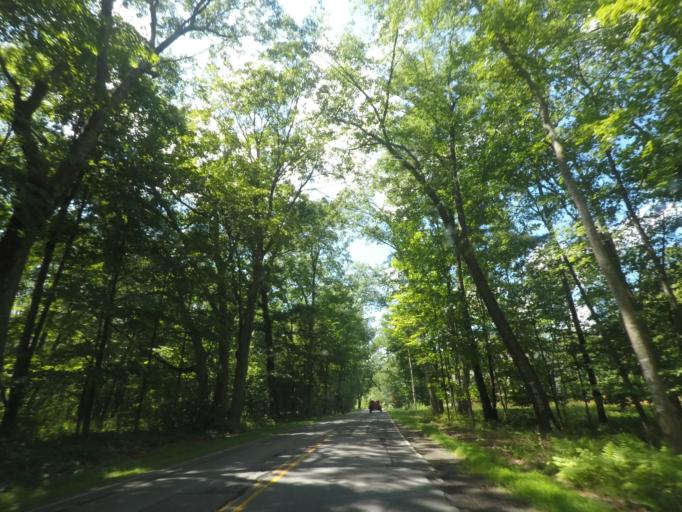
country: US
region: New York
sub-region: Albany County
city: Westmere
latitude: 42.6901
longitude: -73.9072
